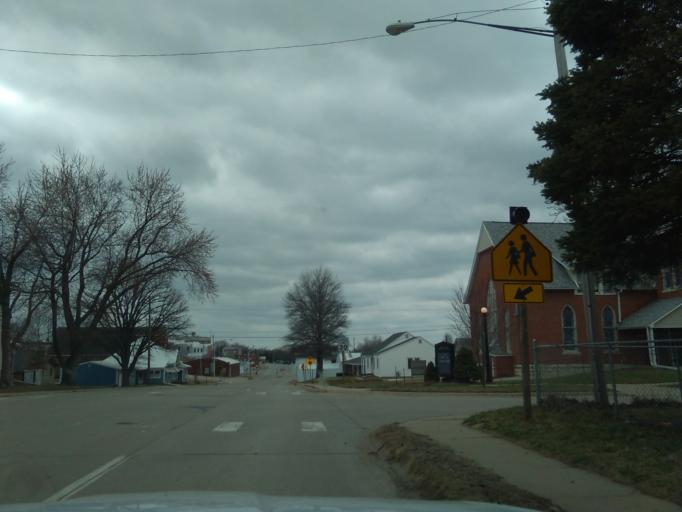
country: US
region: Nebraska
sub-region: Pawnee County
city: Pawnee City
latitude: 40.1118
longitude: -96.1544
